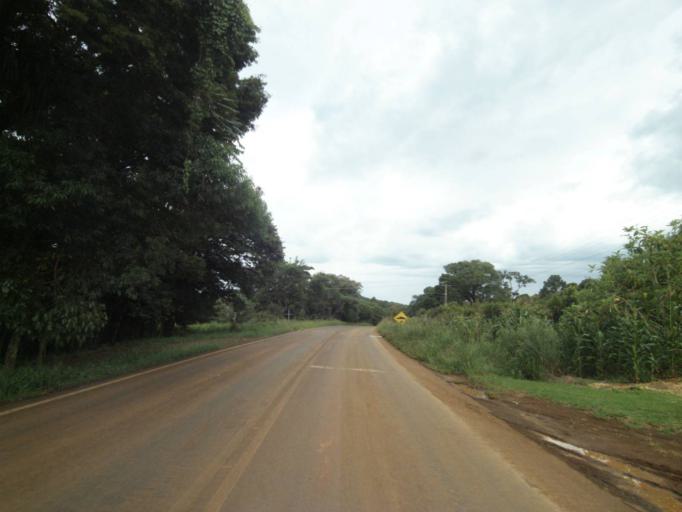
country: BR
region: Parana
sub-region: Pitanga
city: Pitanga
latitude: -24.8950
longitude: -51.9587
